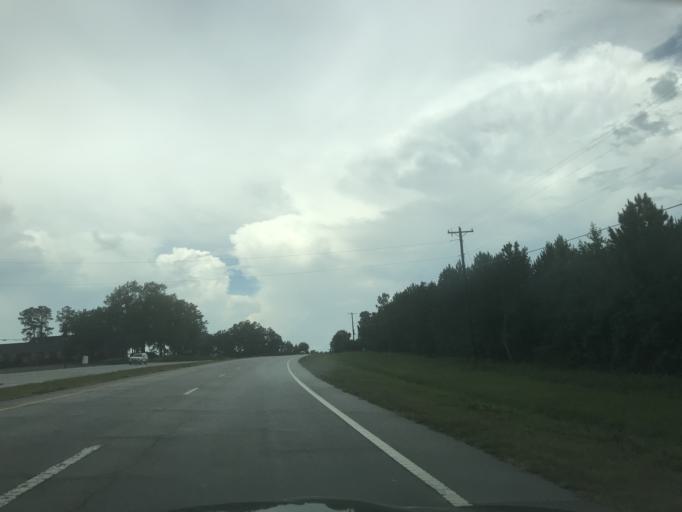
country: US
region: North Carolina
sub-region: Johnston County
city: Wilsons Mills
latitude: 35.5578
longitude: -78.3891
